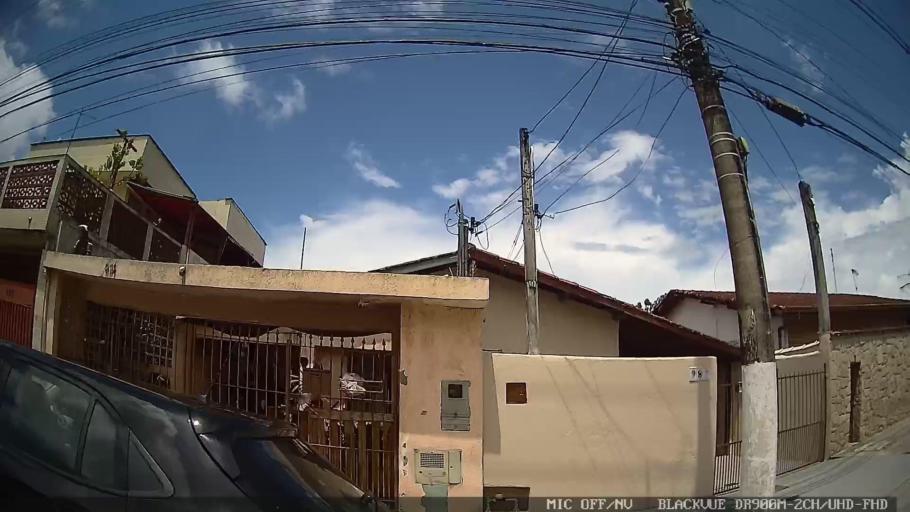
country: BR
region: Sao Paulo
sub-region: Caraguatatuba
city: Caraguatatuba
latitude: -23.6314
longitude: -45.4309
